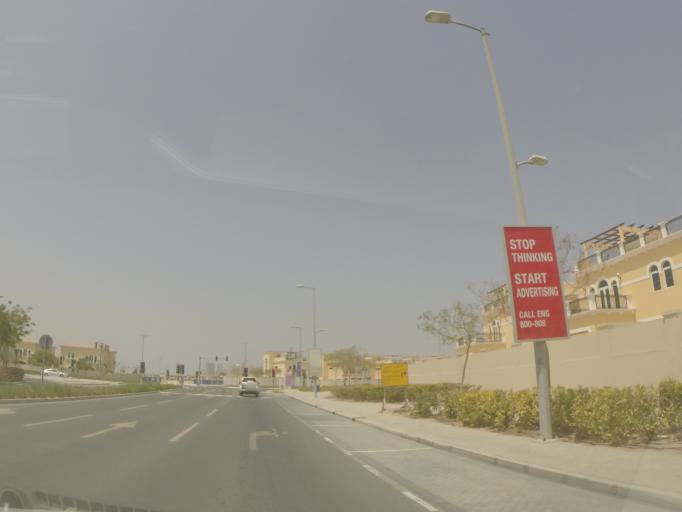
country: AE
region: Dubai
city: Dubai
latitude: 25.0419
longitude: 55.1695
